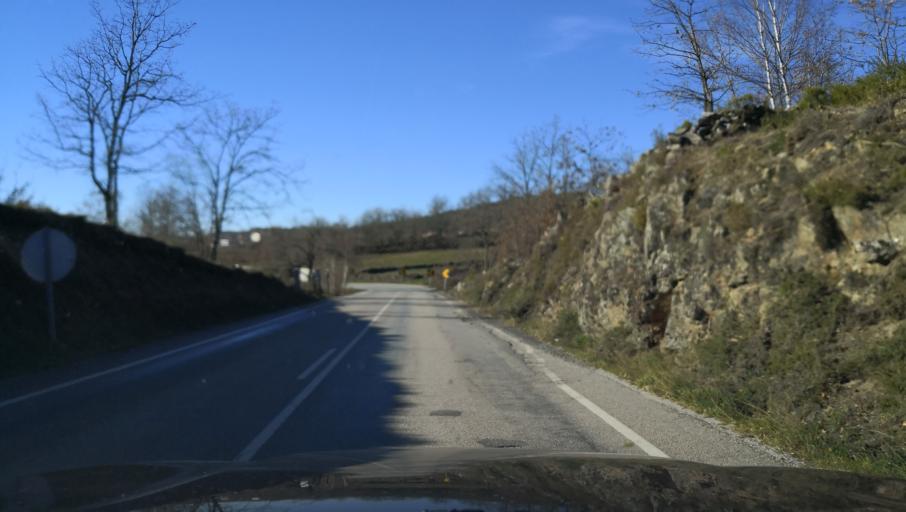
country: PT
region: Vila Real
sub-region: Ribeira de Pena
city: Ribeira de Pena
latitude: 41.5004
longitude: -7.7347
